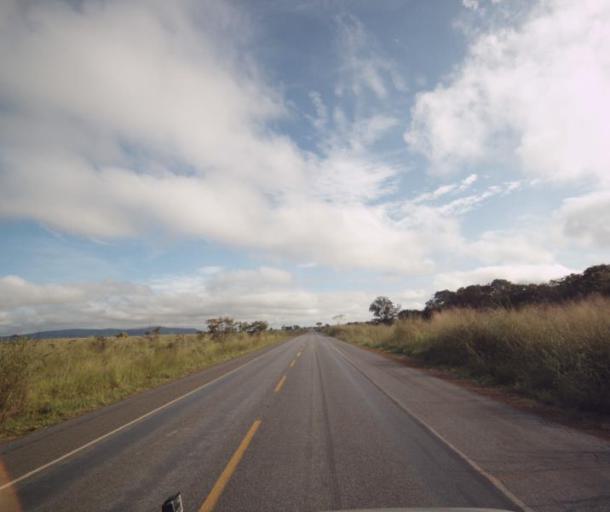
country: BR
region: Goias
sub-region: Padre Bernardo
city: Padre Bernardo
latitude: -15.4594
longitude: -48.6142
